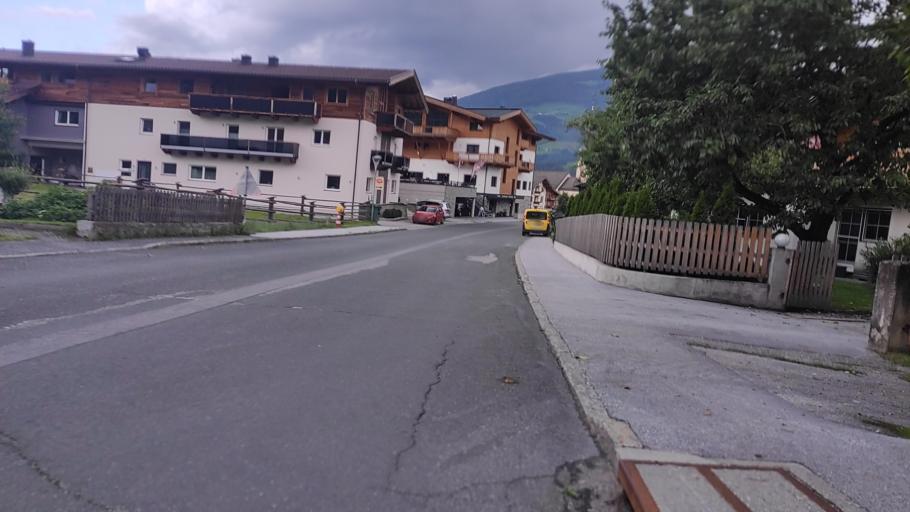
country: AT
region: Salzburg
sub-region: Politischer Bezirk Zell am See
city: Hollersbach im Pinzgau
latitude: 47.2738
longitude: 12.4218
